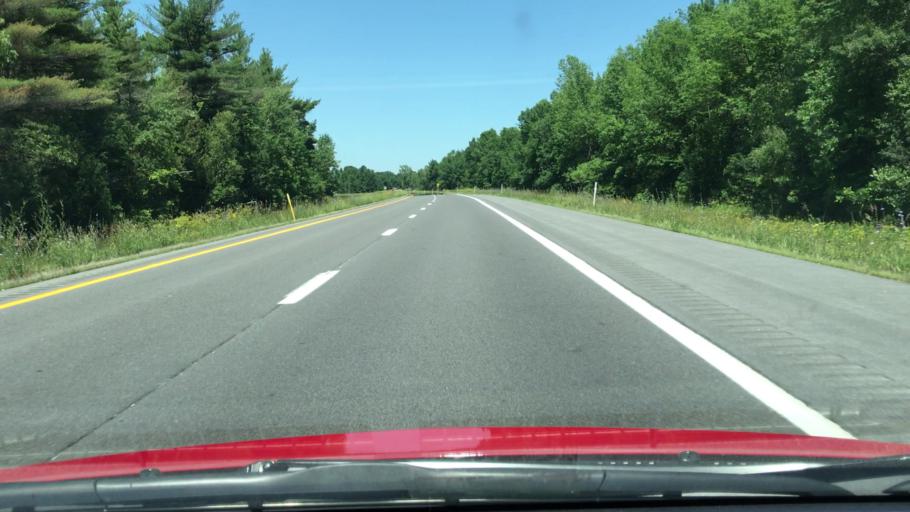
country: US
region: New York
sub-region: Clinton County
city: Cumberland Head
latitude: 44.8437
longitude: -73.4466
